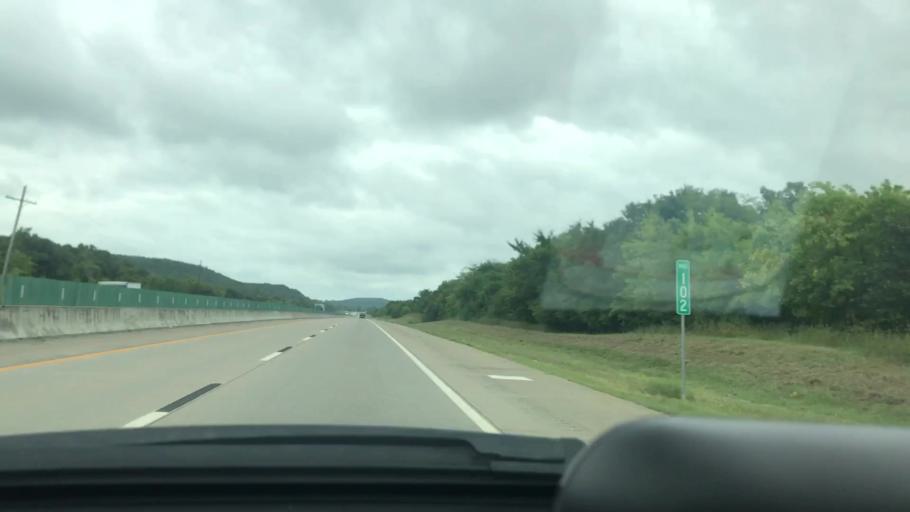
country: US
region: Oklahoma
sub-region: Pittsburg County
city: Krebs
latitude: 35.0750
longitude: -95.7038
